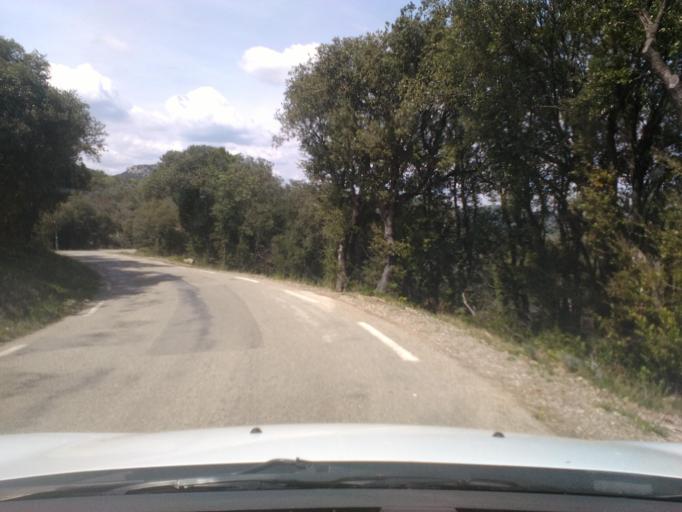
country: FR
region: Languedoc-Roussillon
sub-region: Departement du Gard
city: Saint-Hippolyte-du-Fort
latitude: 43.9771
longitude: 3.8901
